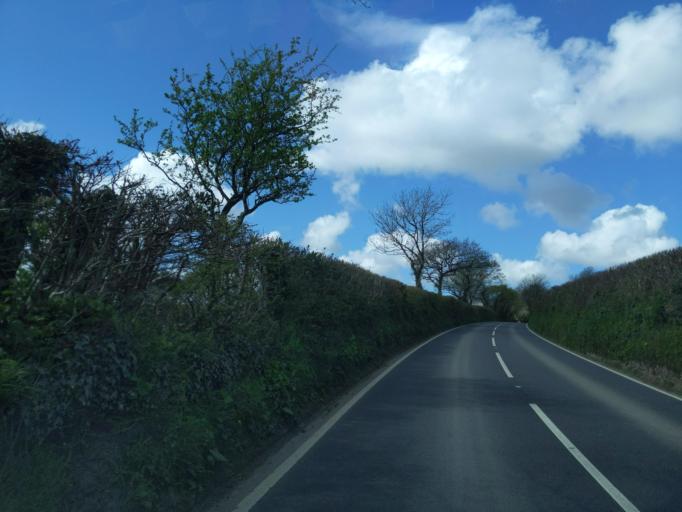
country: GB
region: England
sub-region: Cornwall
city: Bodmin
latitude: 50.4920
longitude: -4.7660
